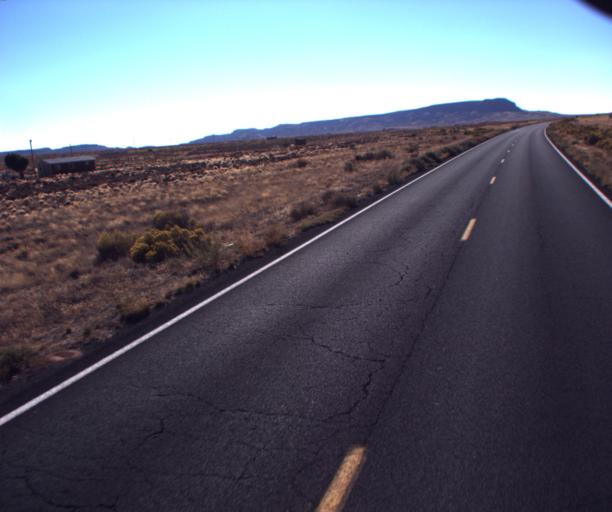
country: US
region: Arizona
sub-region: Navajo County
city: Dilkon
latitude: 35.4713
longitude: -110.4240
